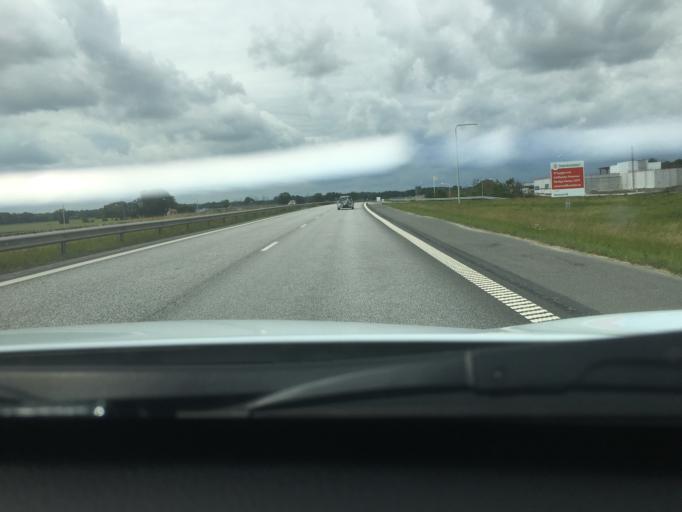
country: SE
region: Skane
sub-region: Kristianstads Kommun
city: Kristianstad
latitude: 56.0258
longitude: 14.2130
